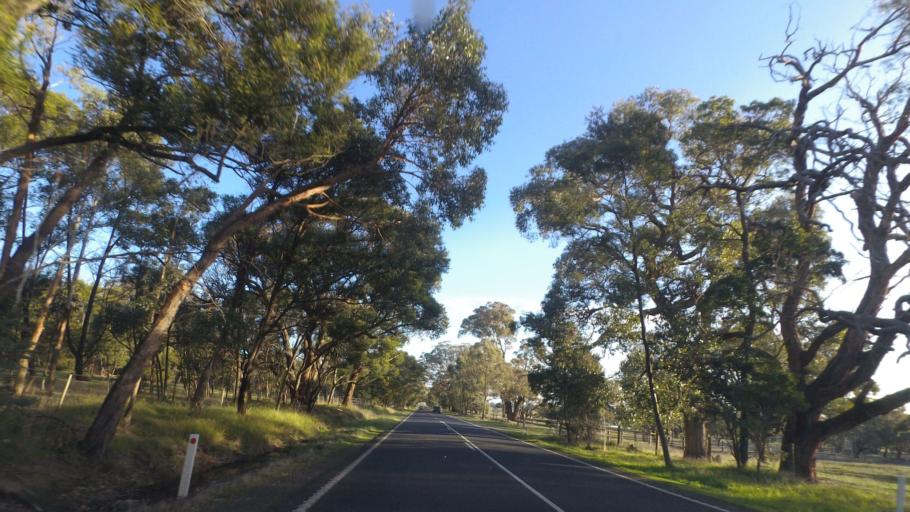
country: AU
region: Victoria
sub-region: Mount Alexander
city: Castlemaine
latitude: -37.1786
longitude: 144.4812
